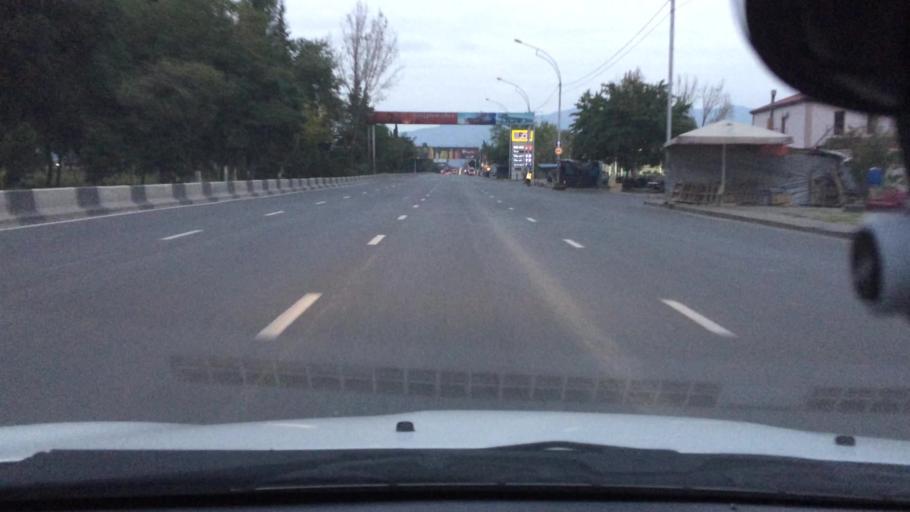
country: GE
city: Zahesi
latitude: 41.7699
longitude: 44.7692
